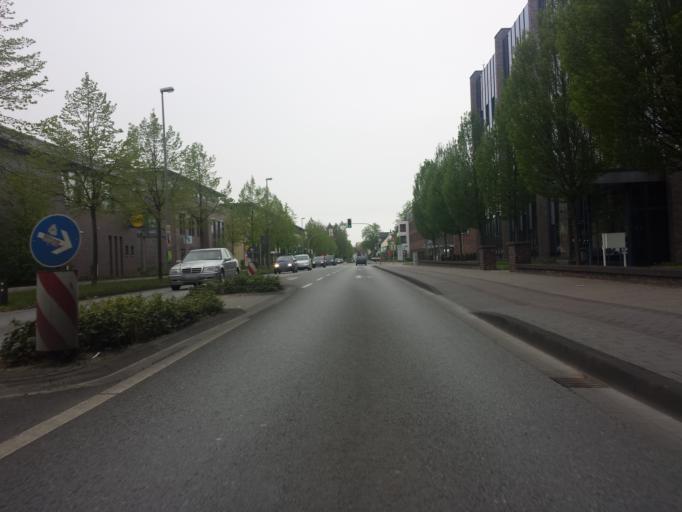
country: DE
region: North Rhine-Westphalia
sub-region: Regierungsbezirk Detmold
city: Guetersloh
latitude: 51.8932
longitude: 8.3824
